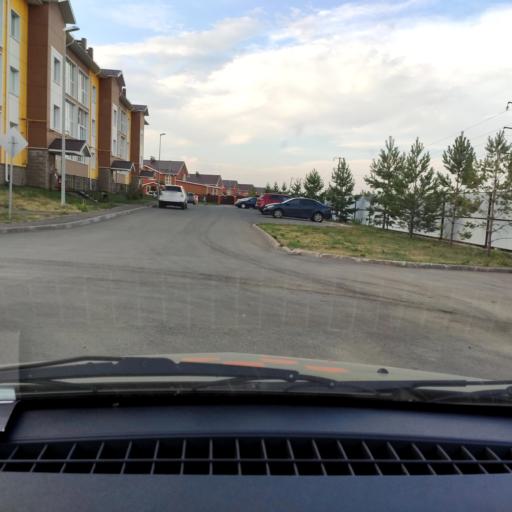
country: RU
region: Bashkortostan
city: Ufa
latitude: 54.5891
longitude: 55.9180
